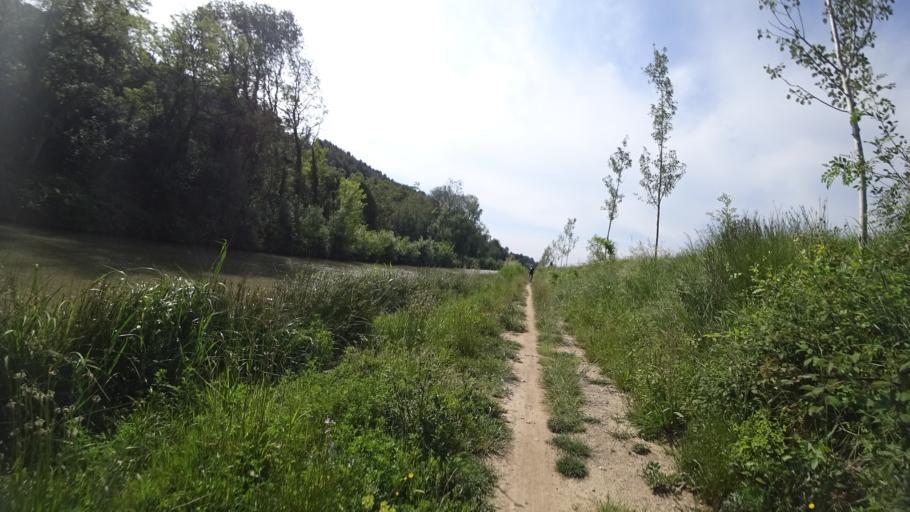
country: FR
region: Languedoc-Roussillon
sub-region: Departement de l'Herault
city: Olonzac
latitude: 43.2570
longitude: 2.7523
